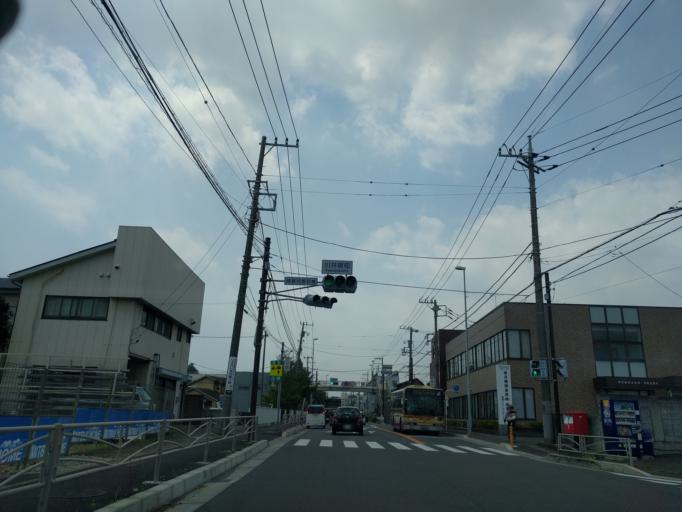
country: JP
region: Kanagawa
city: Minami-rinkan
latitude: 35.4897
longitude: 139.5162
